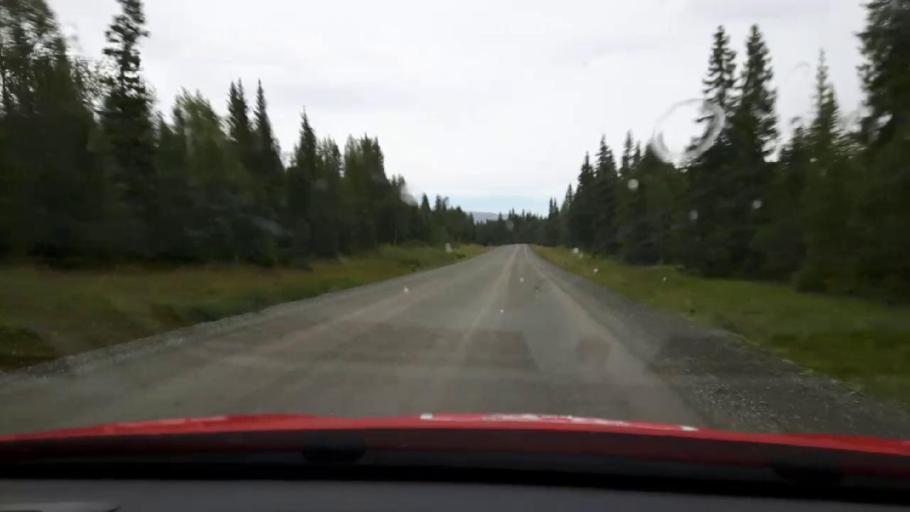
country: SE
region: Jaemtland
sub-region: Are Kommun
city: Are
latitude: 63.4495
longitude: 12.6589
